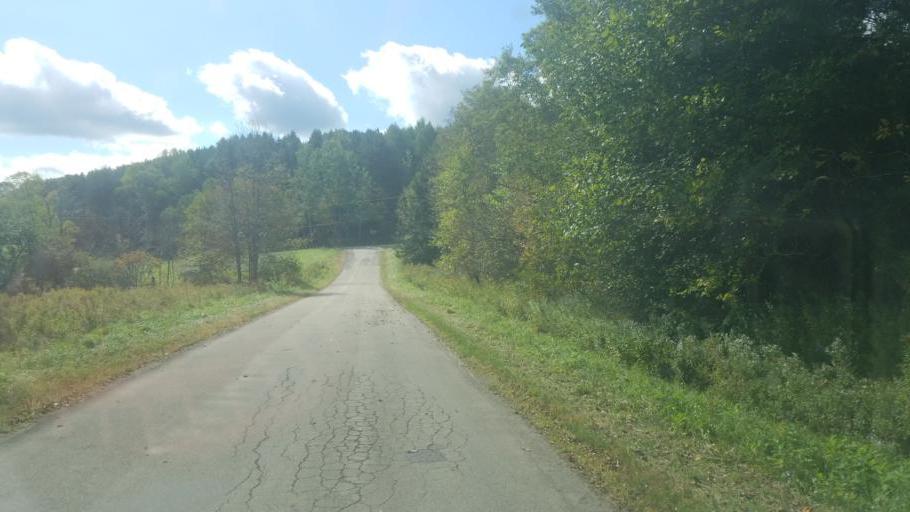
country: US
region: New York
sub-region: Cattaraugus County
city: Olean
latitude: 42.2096
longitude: -78.4148
